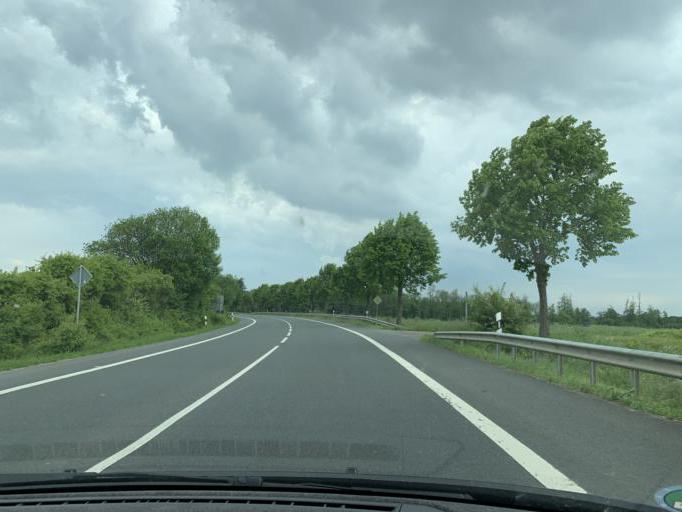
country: DE
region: North Rhine-Westphalia
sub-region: Regierungsbezirk Koln
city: Vettweiss
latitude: 50.7584
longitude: 6.6355
